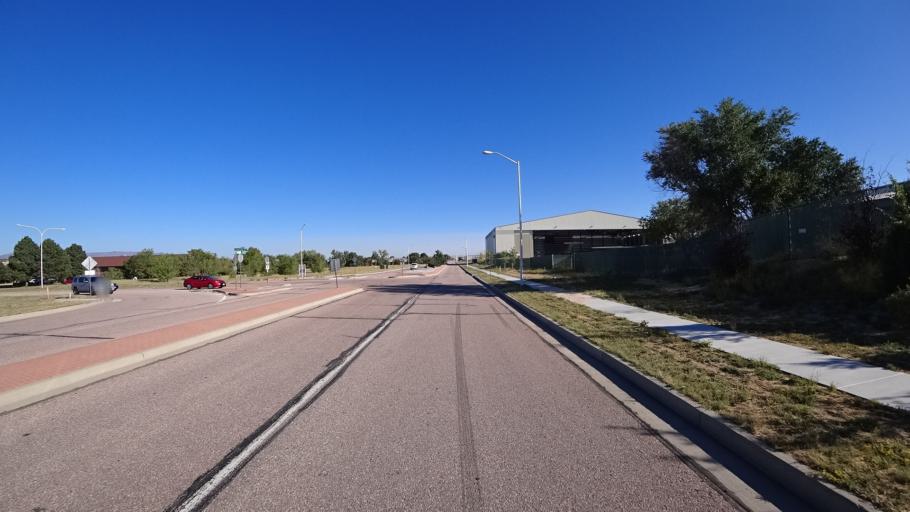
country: US
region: Colorado
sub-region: El Paso County
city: Cimarron Hills
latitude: 38.8058
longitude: -104.7237
